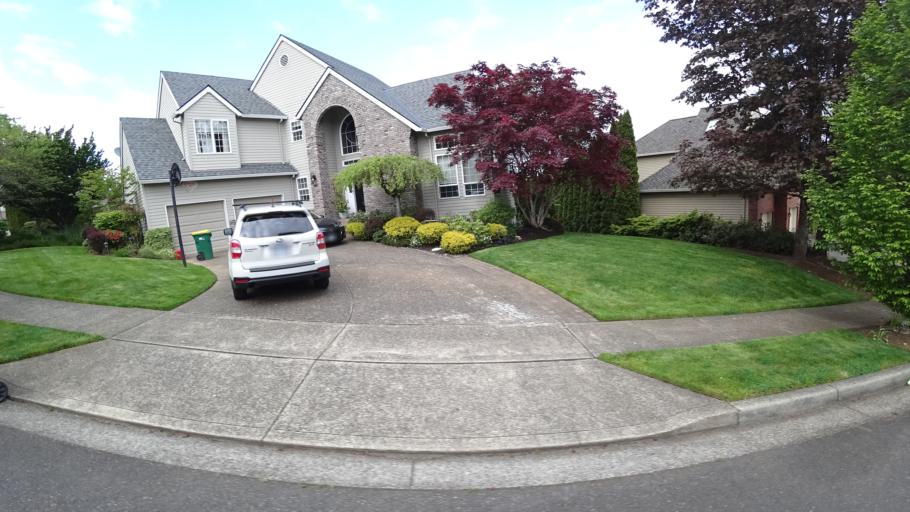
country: US
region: Oregon
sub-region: Washington County
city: Beaverton
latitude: 45.4483
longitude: -122.8399
